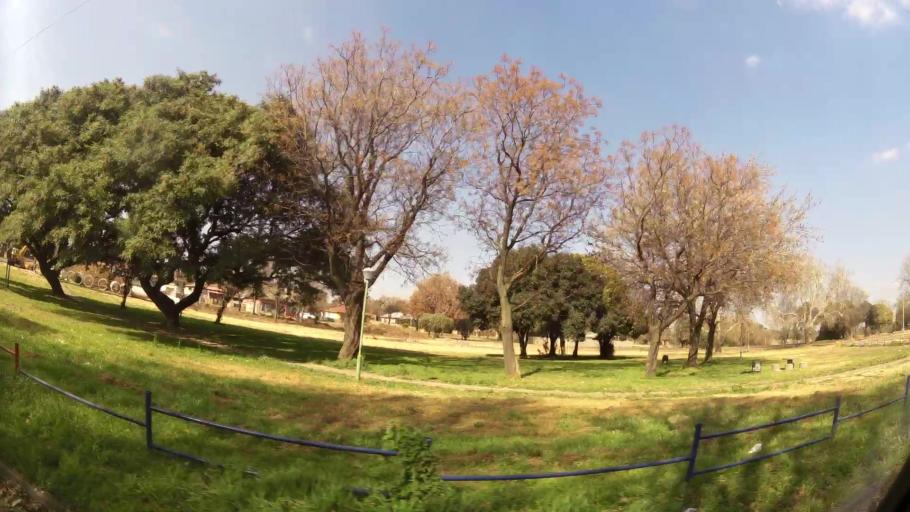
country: ZA
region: Gauteng
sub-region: Ekurhuleni Metropolitan Municipality
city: Germiston
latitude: -26.1839
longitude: 28.2030
